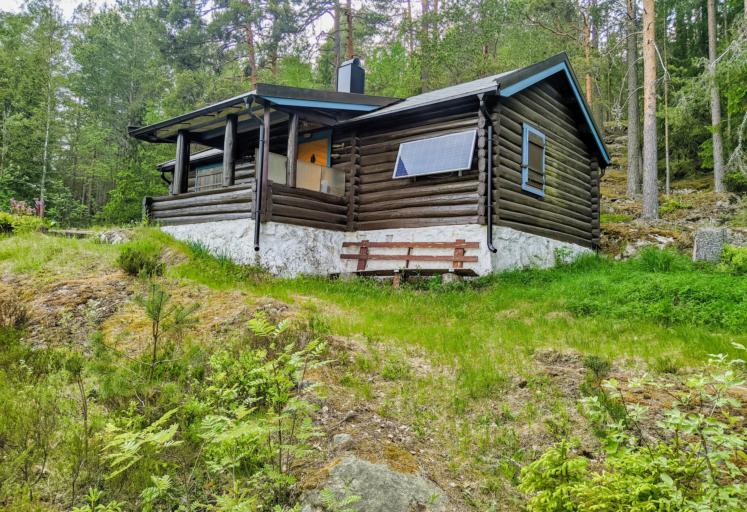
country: NO
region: Akershus
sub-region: Sorum
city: Sorumsand
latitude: 59.9475
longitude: 11.2350
